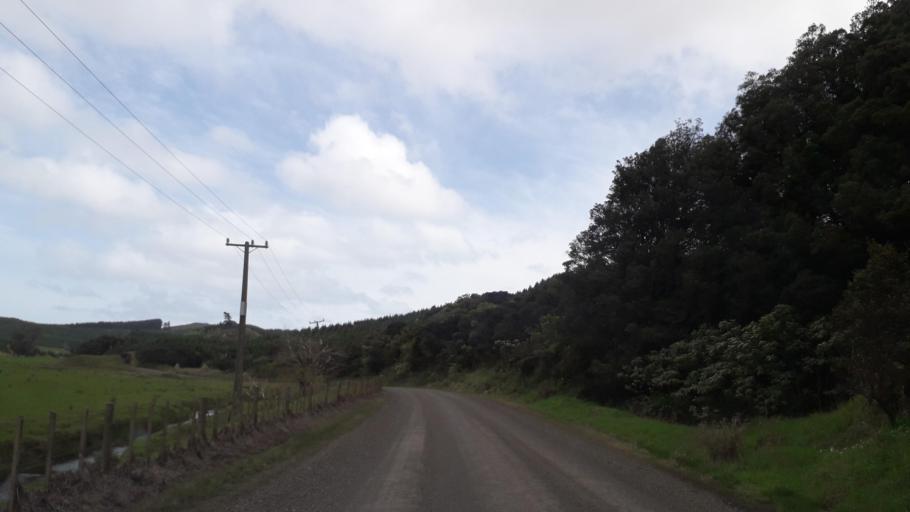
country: NZ
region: Northland
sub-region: Far North District
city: Ahipara
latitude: -35.4275
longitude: 173.3544
